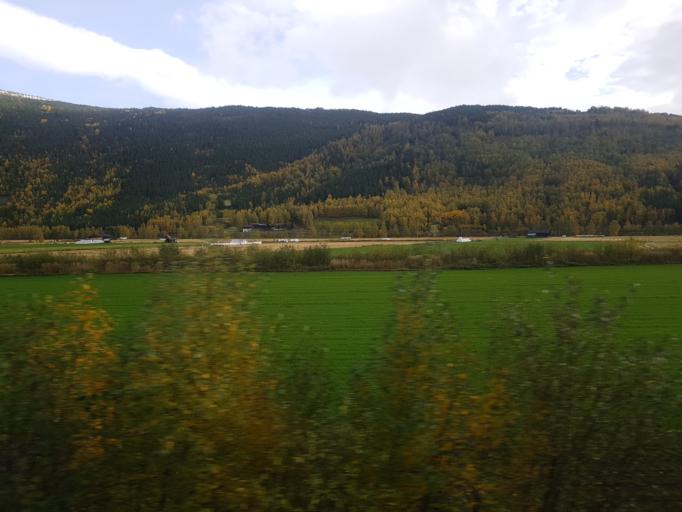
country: NO
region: Oppland
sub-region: Sel
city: Otta
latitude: 61.8074
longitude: 9.5401
